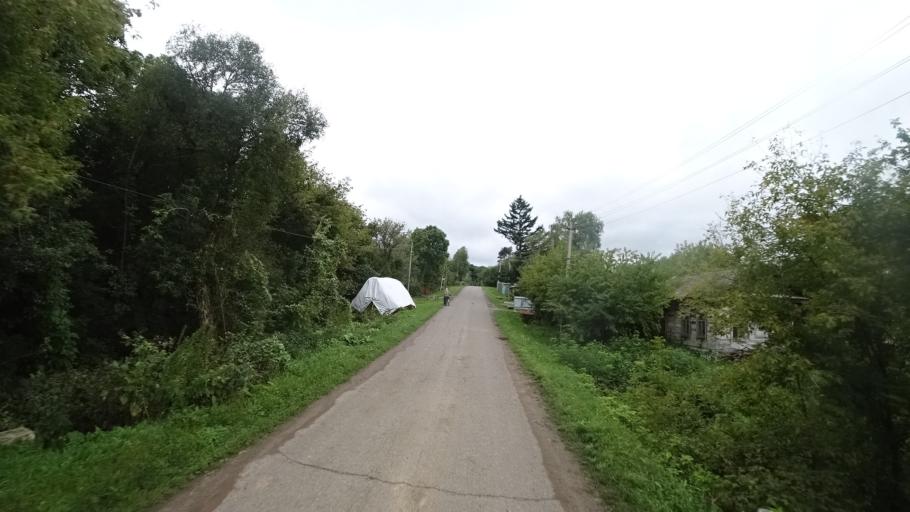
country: RU
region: Primorskiy
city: Chernigovka
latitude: 44.4550
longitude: 132.5881
